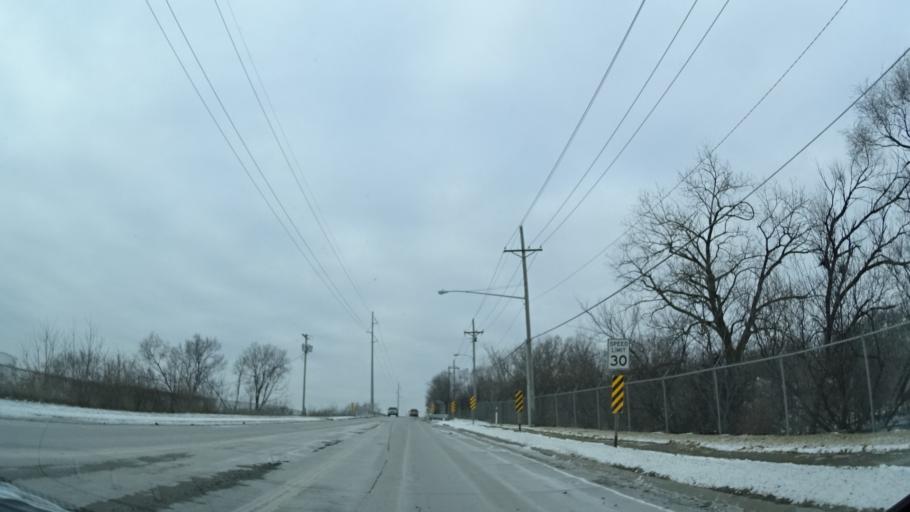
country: US
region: Nebraska
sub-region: Douglas County
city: Omaha
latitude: 41.2198
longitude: -95.9609
